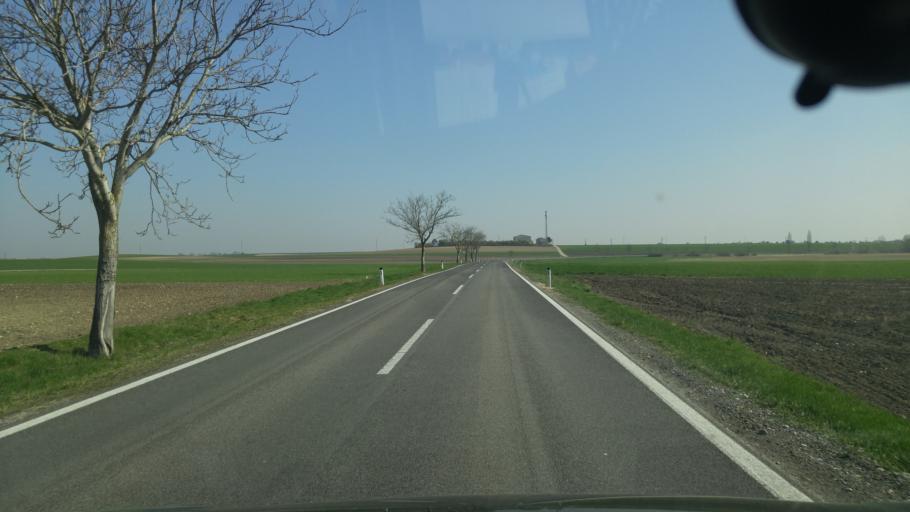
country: AT
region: Lower Austria
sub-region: Politischer Bezirk Wien-Umgebung
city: Moosbrunn
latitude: 48.0160
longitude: 16.4395
